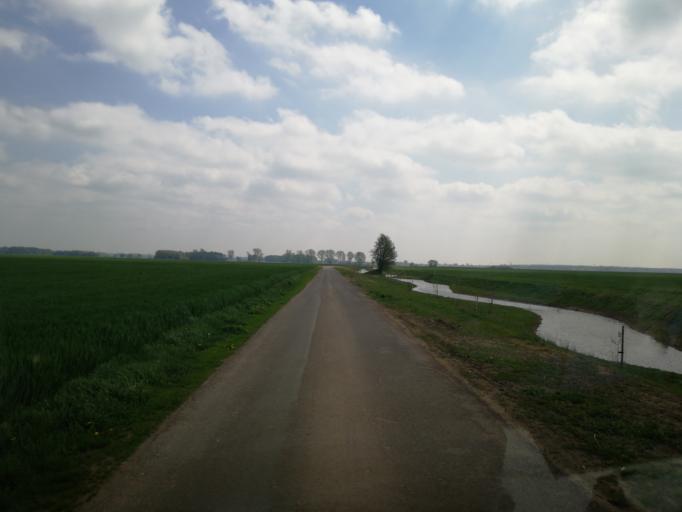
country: DE
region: Brandenburg
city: Doberlug-Kirchhain
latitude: 51.6869
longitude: 13.5319
